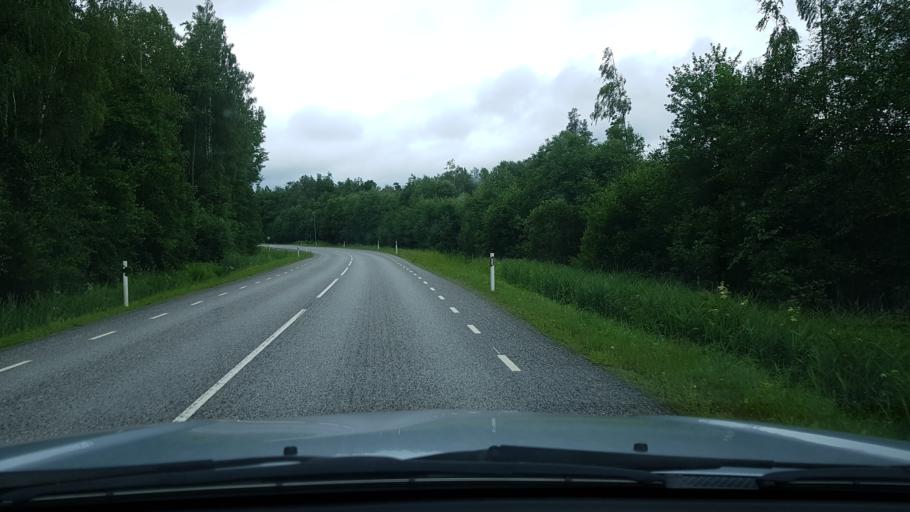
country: EE
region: Ida-Virumaa
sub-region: Narva-Joesuu linn
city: Narva-Joesuu
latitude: 59.3595
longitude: 27.9288
